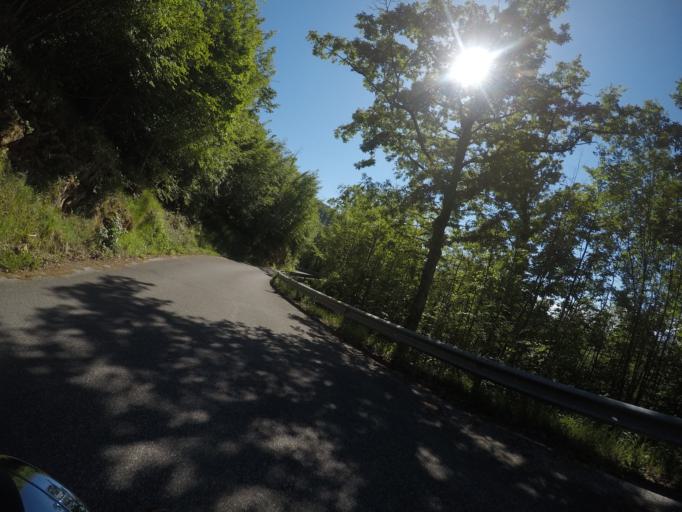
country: IT
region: Tuscany
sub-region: Provincia di Massa-Carrara
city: Fosdinovo
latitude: 44.1328
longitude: 10.0698
